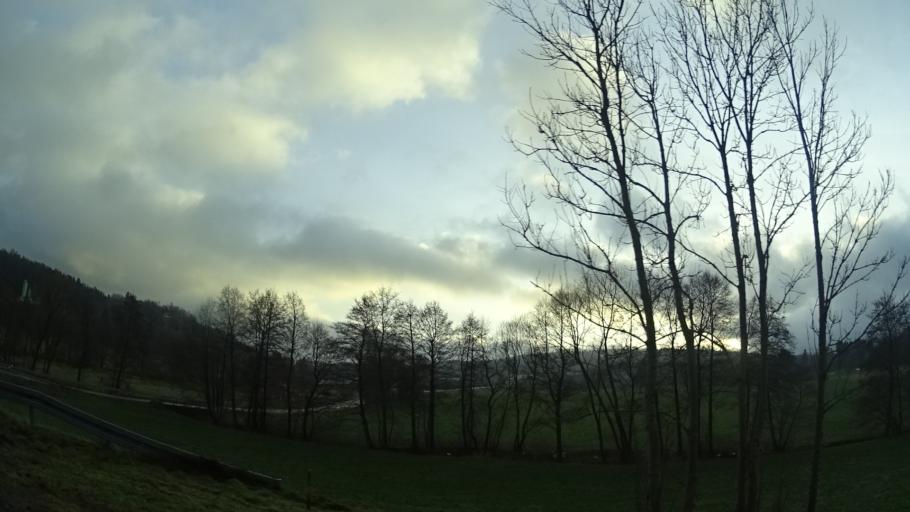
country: DE
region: Hesse
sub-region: Regierungsbezirk Kassel
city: Hilders
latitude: 50.5591
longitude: 9.9356
